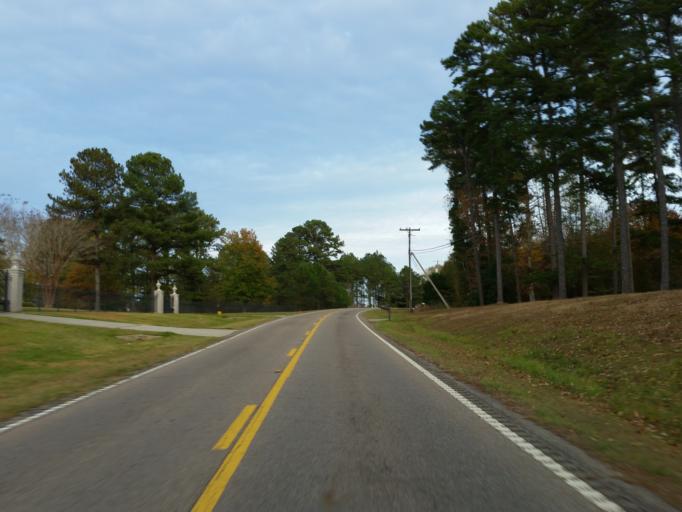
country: US
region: Mississippi
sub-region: Lauderdale County
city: Marion
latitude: 32.4109
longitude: -88.5738
